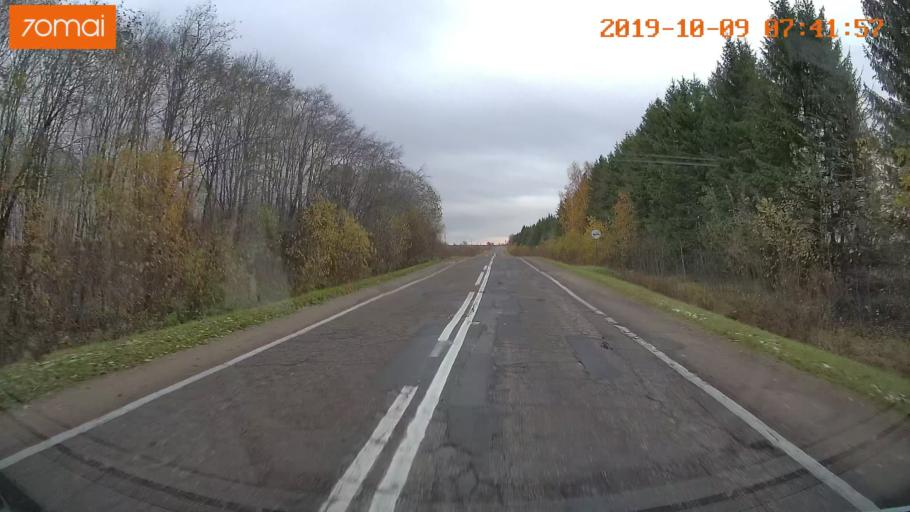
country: RU
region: Jaroslavl
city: Kukoboy
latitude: 58.6409
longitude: 39.7146
